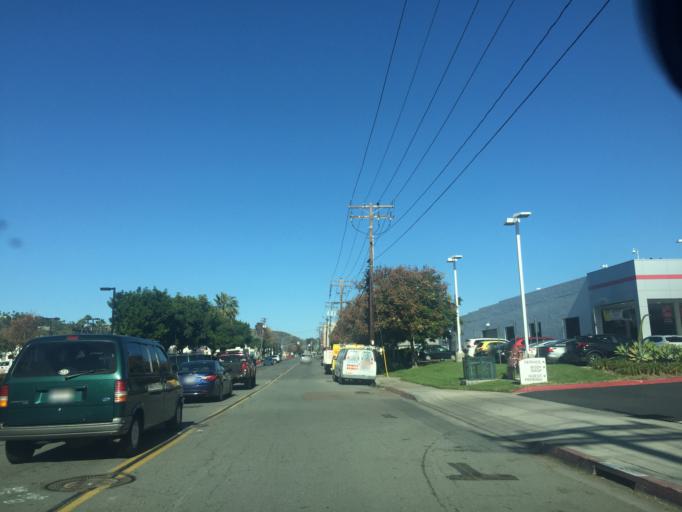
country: US
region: California
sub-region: San Diego County
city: La Mesa
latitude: 32.7822
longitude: -117.1015
